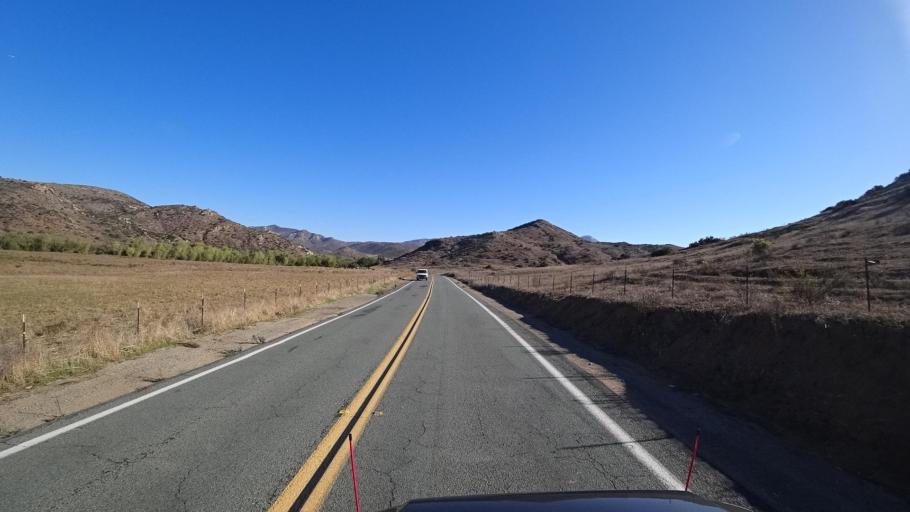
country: US
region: California
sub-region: San Diego County
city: Jamul
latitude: 32.6601
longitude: -116.8393
